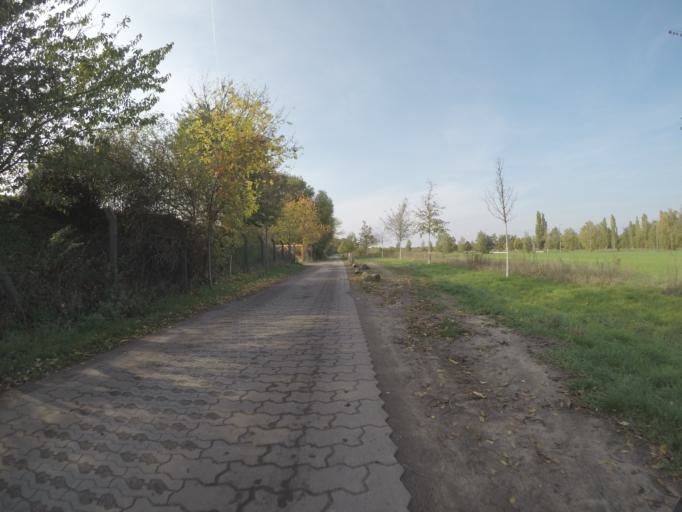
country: DE
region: Berlin
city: Rudow
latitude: 52.3942
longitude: 13.4813
